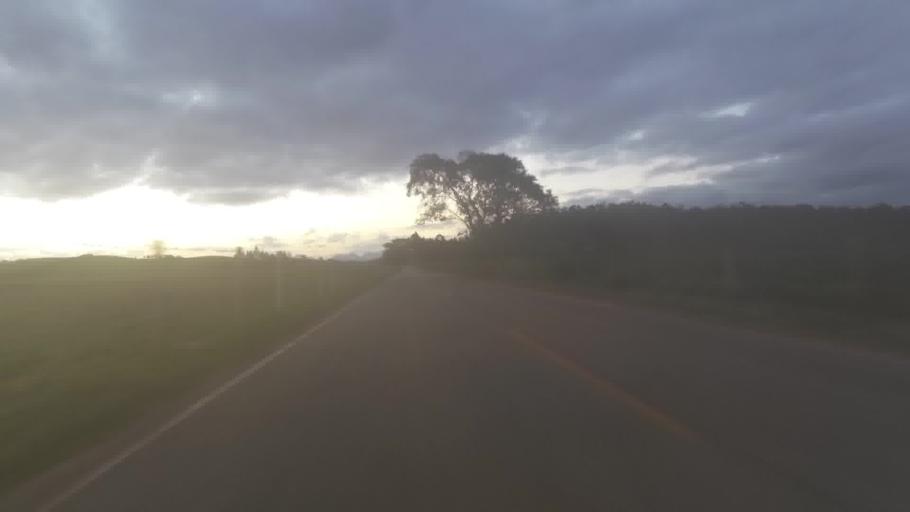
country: BR
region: Espirito Santo
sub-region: Itapemirim
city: Itapemirim
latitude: -20.9734
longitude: -40.8669
